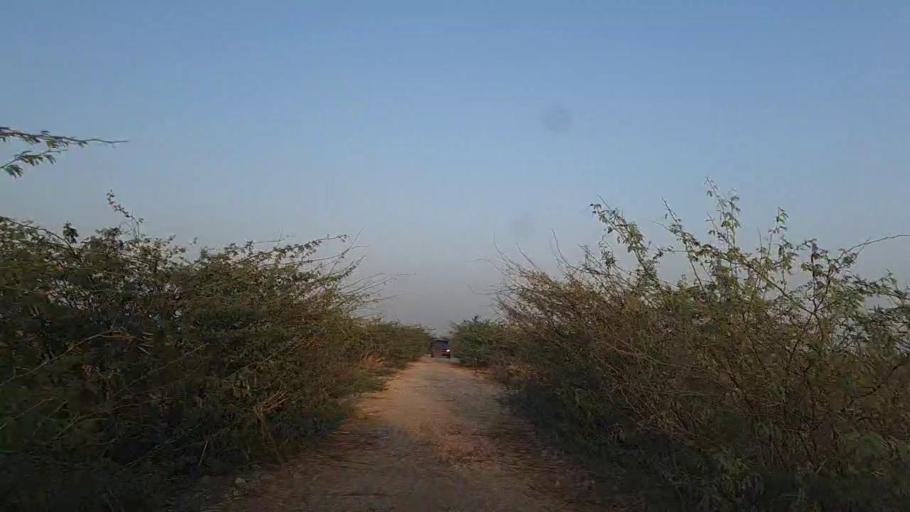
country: PK
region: Sindh
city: Naukot
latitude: 24.6980
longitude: 69.2565
